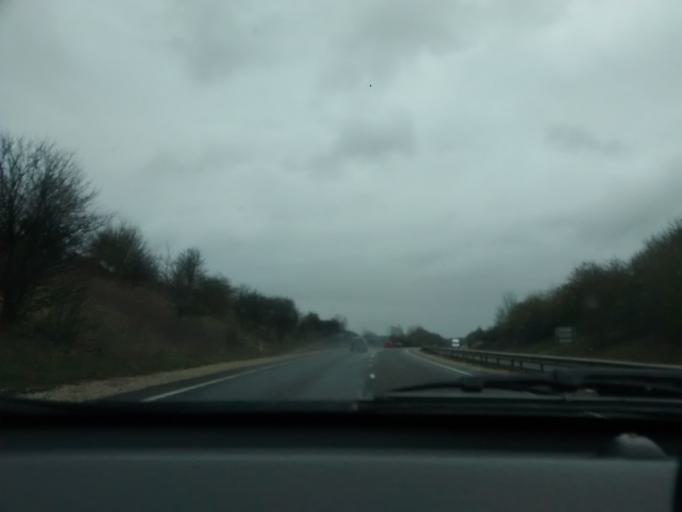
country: GB
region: England
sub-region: Suffolk
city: Needham Market
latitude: 52.1755
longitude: 1.0504
